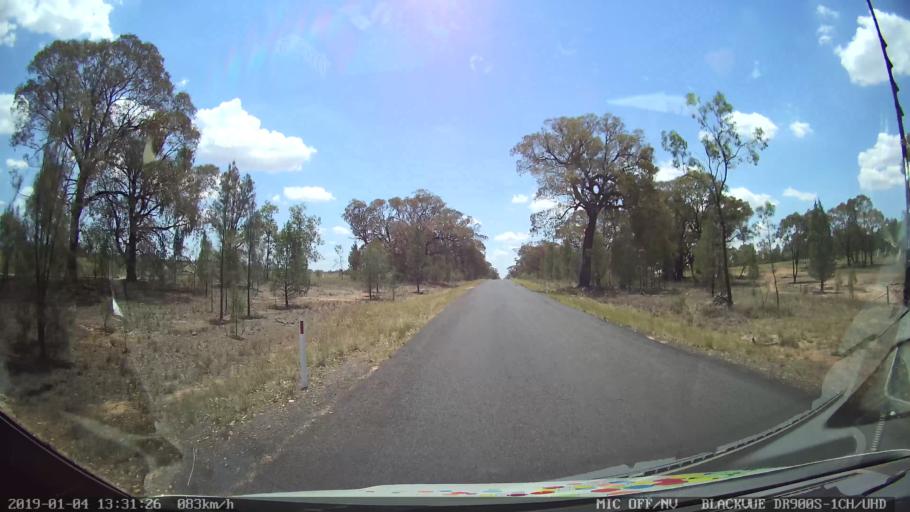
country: AU
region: New South Wales
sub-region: Parkes
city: Peak Hill
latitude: -32.6227
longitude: 148.5487
